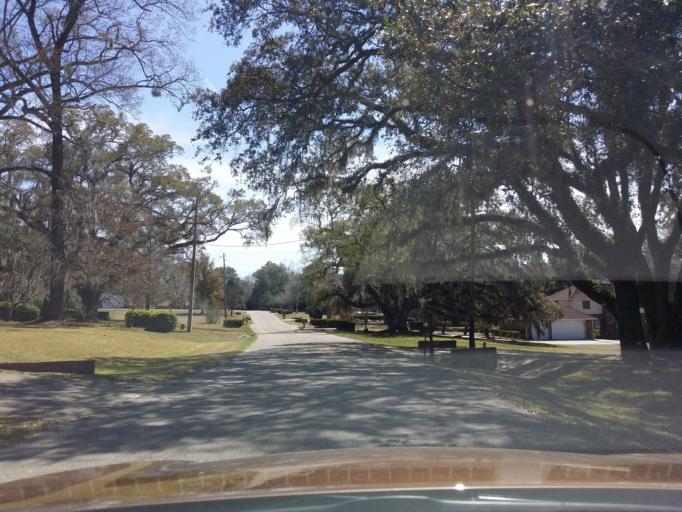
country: US
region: Florida
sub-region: Leon County
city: Tallahassee
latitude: 30.4811
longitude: -84.1873
